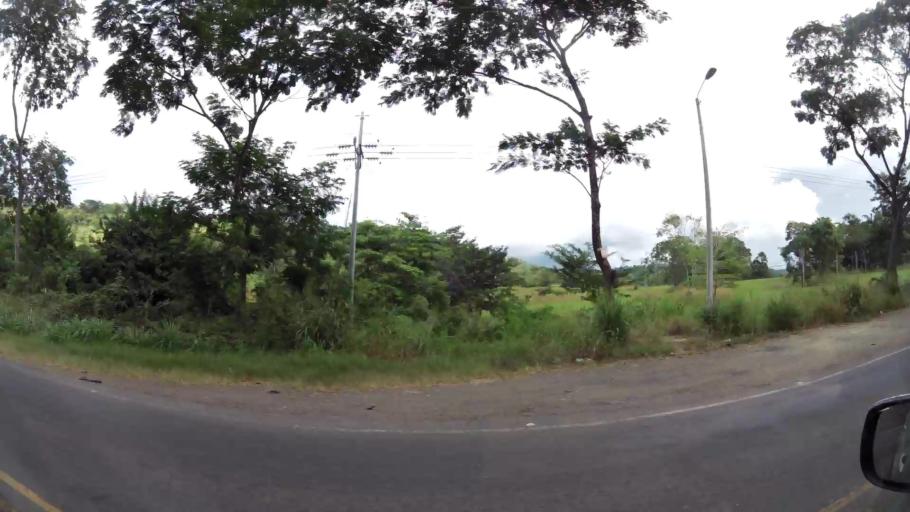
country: CR
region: Guanacaste
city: Juntas
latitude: 10.1690
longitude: -84.9213
